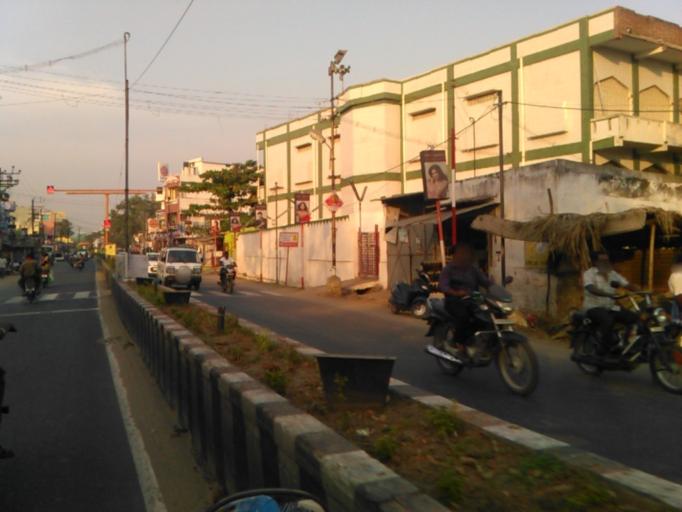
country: IN
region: Tamil Nadu
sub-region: Erode
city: Erode
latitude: 11.3470
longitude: 77.7311
